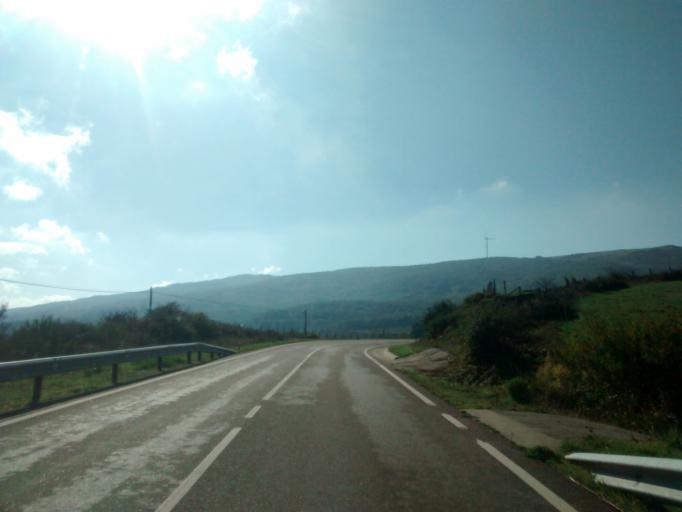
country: ES
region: Cantabria
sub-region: Provincia de Cantabria
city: Reinosa
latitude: 42.9828
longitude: -4.1045
